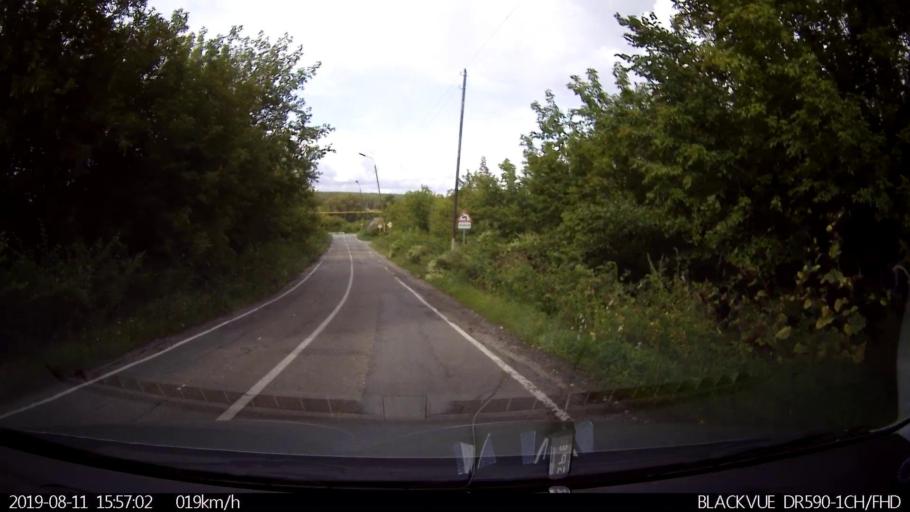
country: RU
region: Ulyanovsk
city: Ignatovka
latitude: 53.9492
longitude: 47.6525
